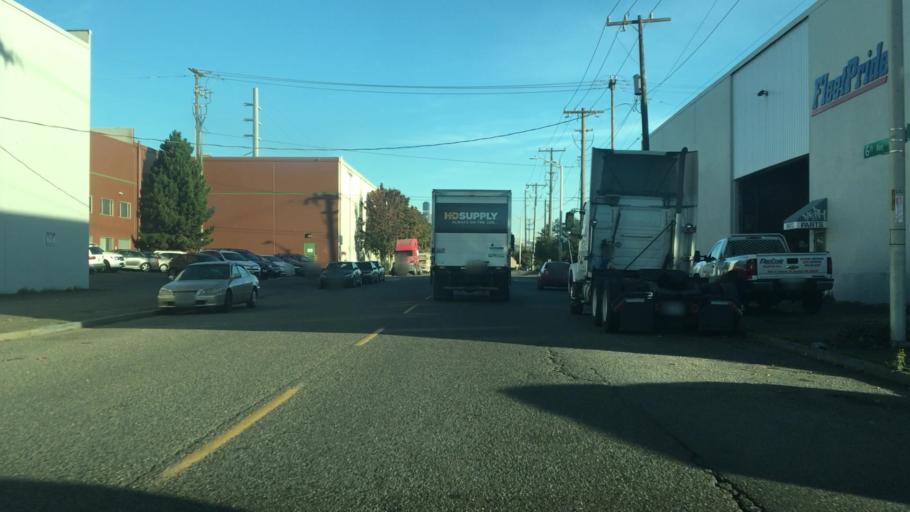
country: US
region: Washington
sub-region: King County
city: Seattle
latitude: 47.5673
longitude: -122.3267
